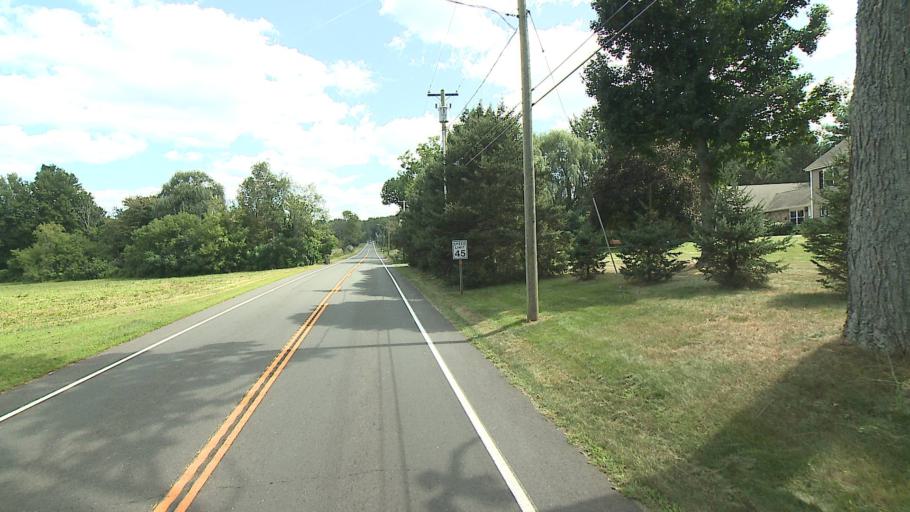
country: US
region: Connecticut
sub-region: Tolland County
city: Ellington
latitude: 41.9111
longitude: -72.4531
